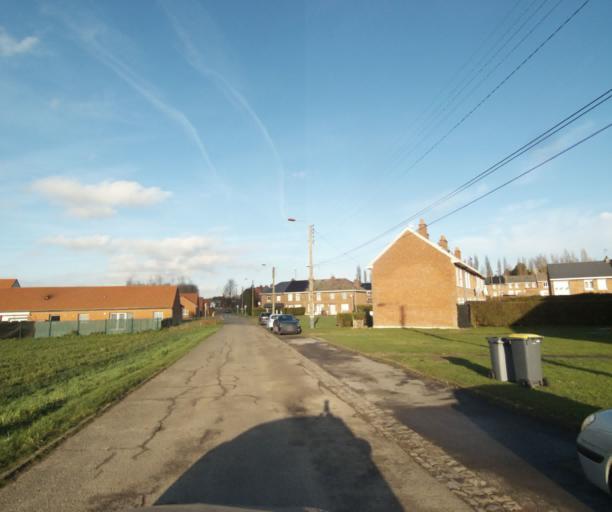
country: FR
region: Nord-Pas-de-Calais
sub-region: Departement du Nord
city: Marly
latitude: 50.3415
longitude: 3.5444
